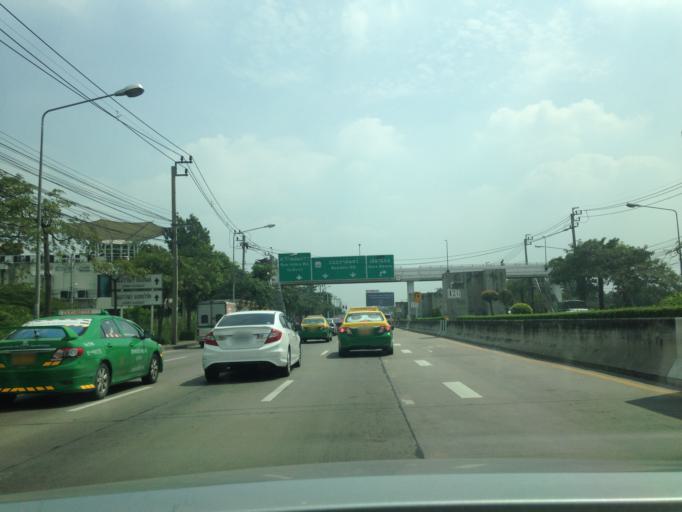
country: TH
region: Bangkok
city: Lat Phrao
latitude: 13.8339
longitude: 100.6094
